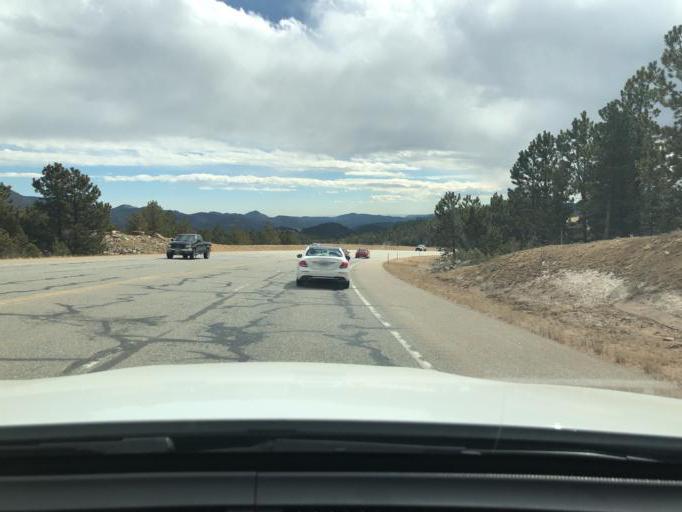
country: US
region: Colorado
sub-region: Gilpin County
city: Central City
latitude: 39.7889
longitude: -105.4993
